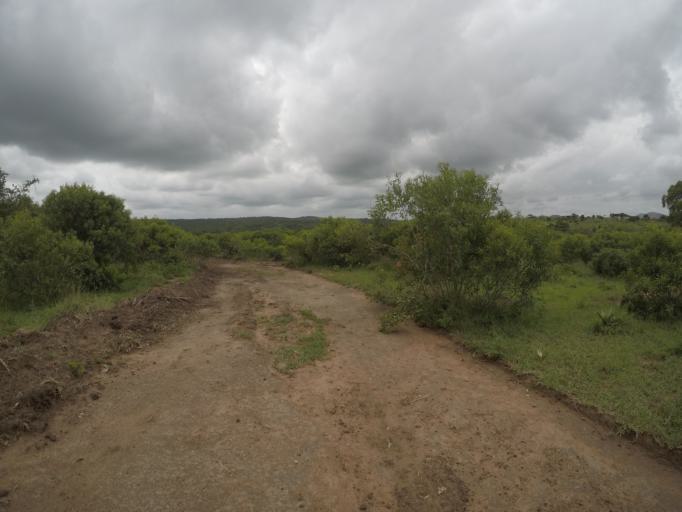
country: ZA
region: KwaZulu-Natal
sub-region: uThungulu District Municipality
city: Empangeni
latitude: -28.6013
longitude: 31.8295
